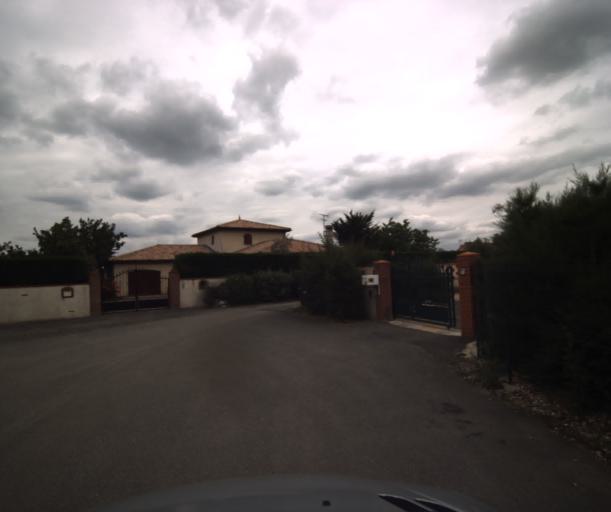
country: FR
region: Midi-Pyrenees
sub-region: Departement de la Haute-Garonne
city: Labarthe-sur-Leze
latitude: 43.4609
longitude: 1.4022
